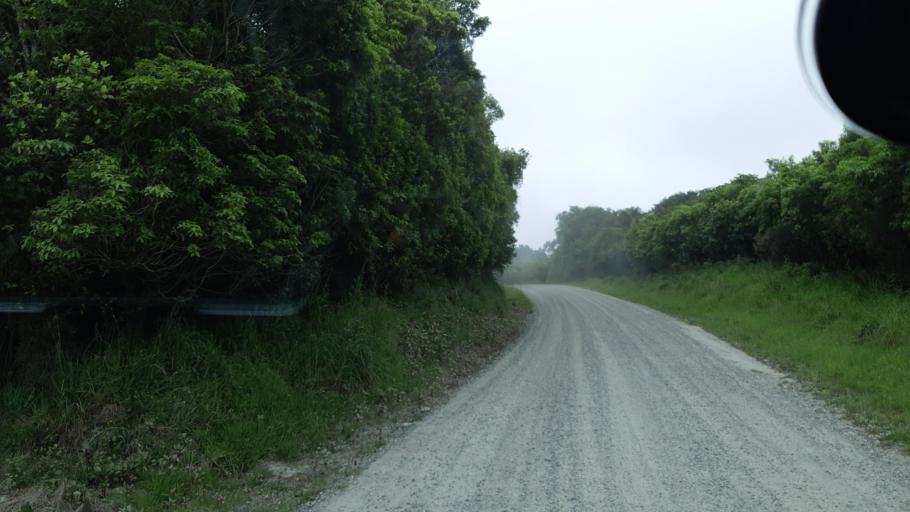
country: NZ
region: West Coast
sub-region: Grey District
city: Greymouth
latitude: -42.6387
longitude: 171.3958
